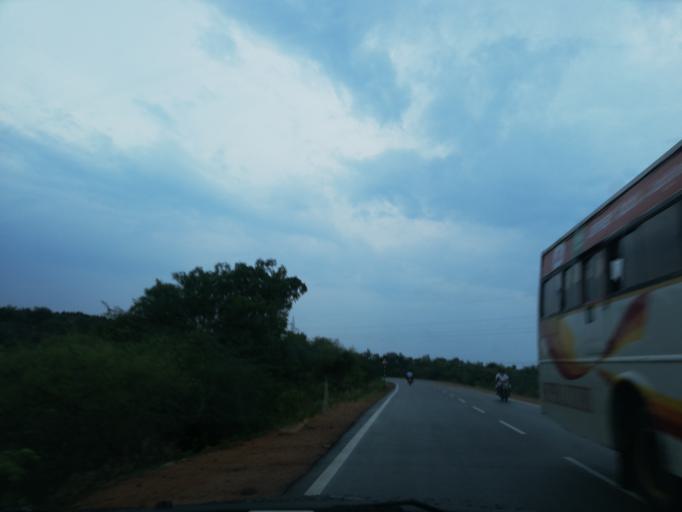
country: IN
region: Andhra Pradesh
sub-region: Guntur
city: Macherla
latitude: 16.6611
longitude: 79.2855
